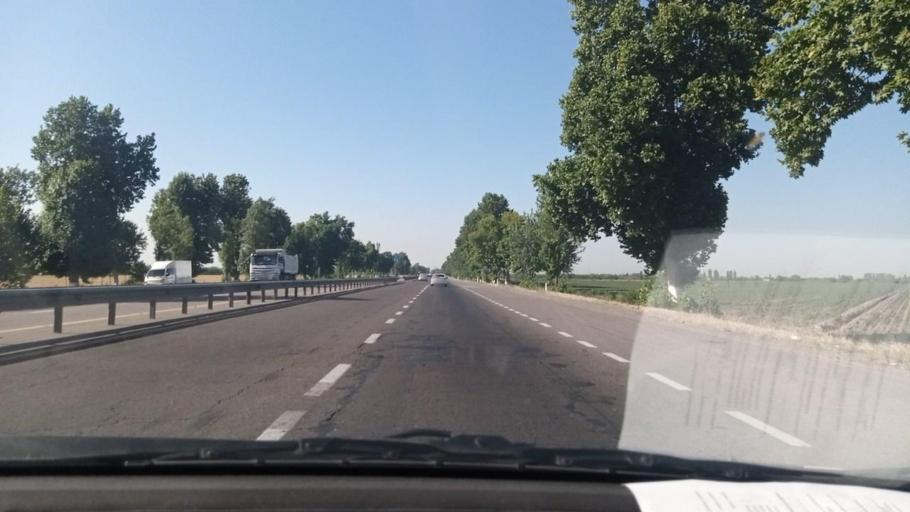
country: UZ
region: Toshkent Shahri
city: Bektemir
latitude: 41.2058
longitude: 69.4028
